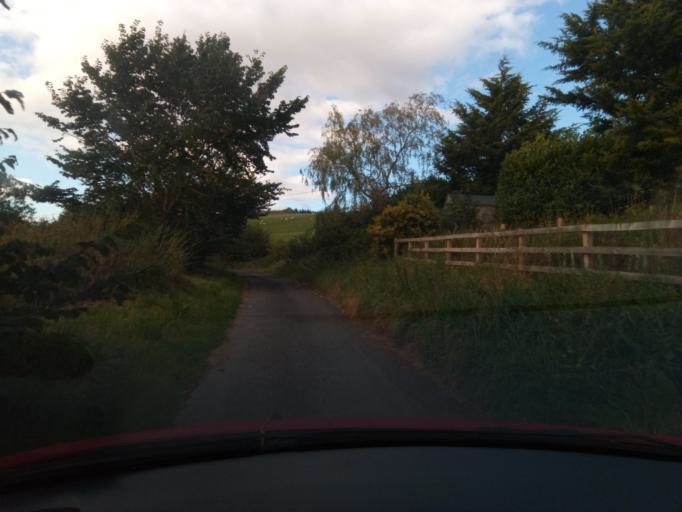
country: GB
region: Scotland
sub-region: The Scottish Borders
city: Kelso
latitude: 55.5263
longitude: -2.3476
